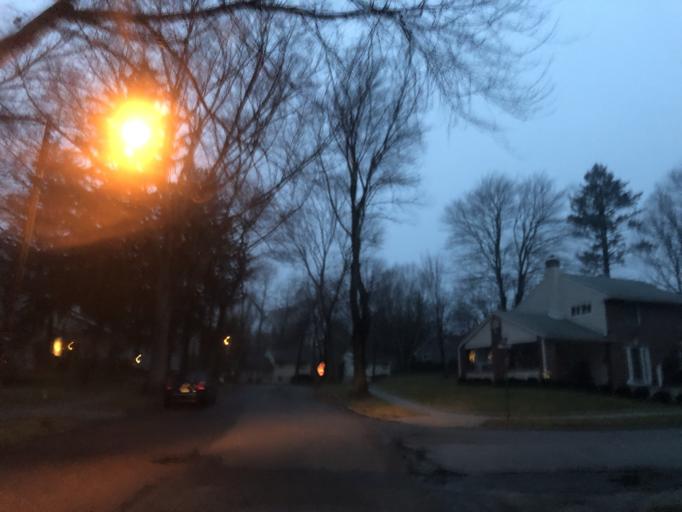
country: US
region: Pennsylvania
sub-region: Delaware County
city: Radnor
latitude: 40.0228
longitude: -75.3418
